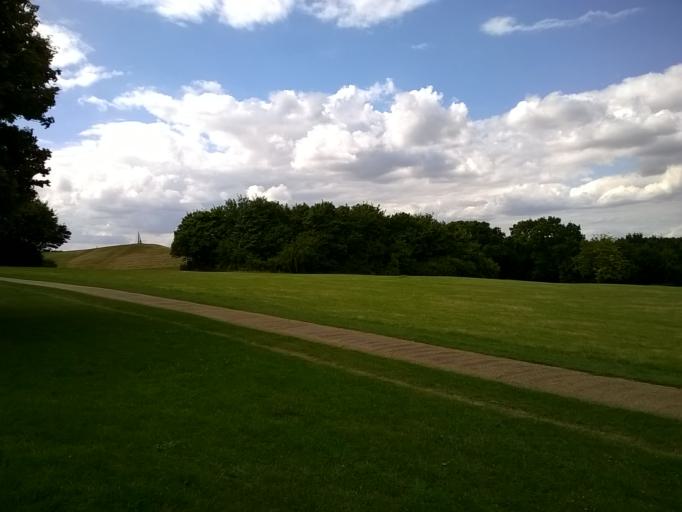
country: GB
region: England
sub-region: Milton Keynes
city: Milton Keynes
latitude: 52.0475
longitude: -0.7399
